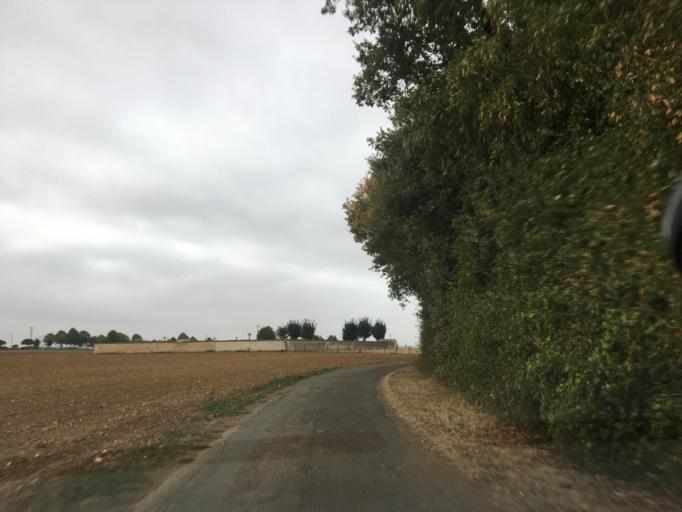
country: FR
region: Poitou-Charentes
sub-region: Departement des Deux-Sevres
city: Beauvoir-sur-Niort
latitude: 46.0785
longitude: -0.5210
